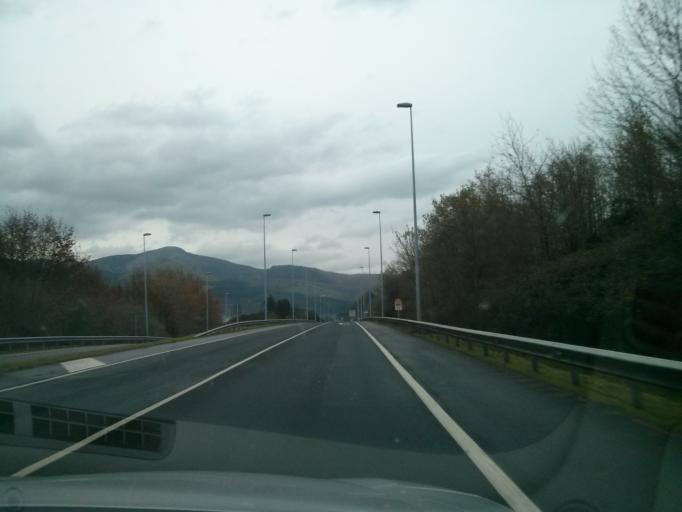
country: ES
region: Basque Country
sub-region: Bizkaia
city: El Corrillo
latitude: 43.2050
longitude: -3.1273
